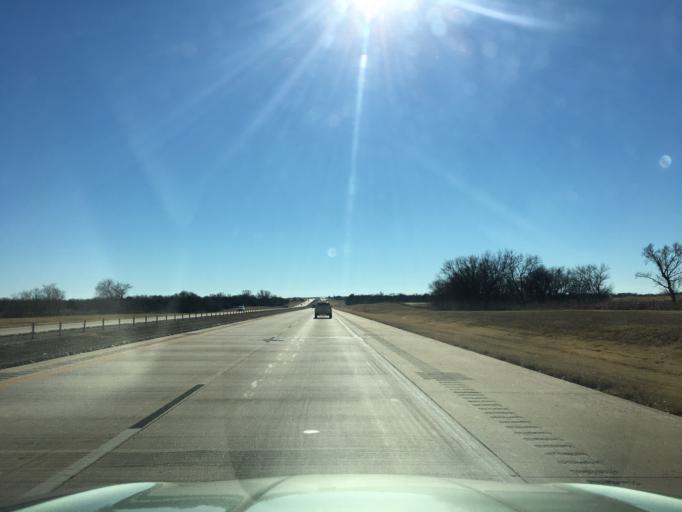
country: US
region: Oklahoma
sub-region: Noble County
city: Perry
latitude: 36.4438
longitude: -97.3271
